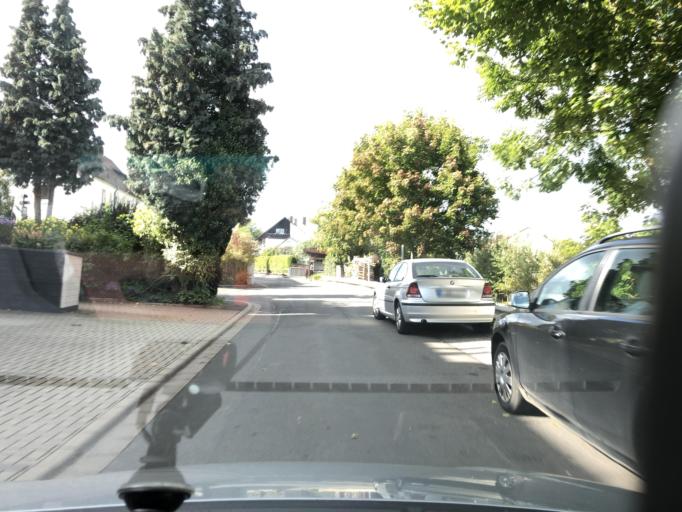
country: DE
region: Bavaria
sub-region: Regierungsbezirk Mittelfranken
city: Langenzenn
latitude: 49.4980
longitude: 10.8083
